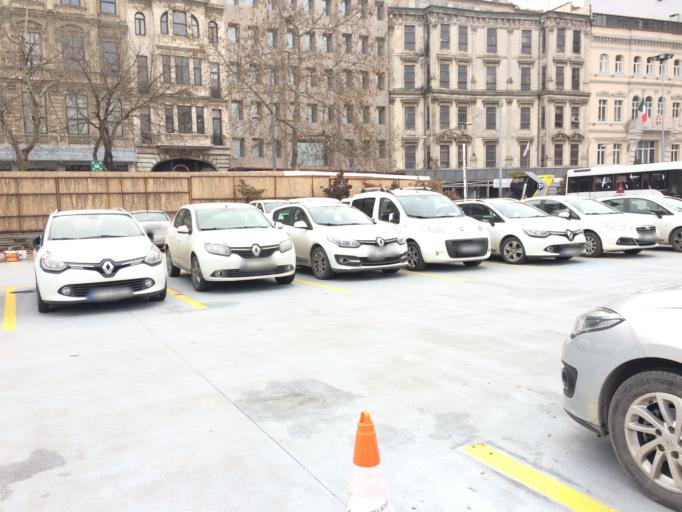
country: TR
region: Istanbul
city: Eminoenue
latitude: 41.0319
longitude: 28.9744
